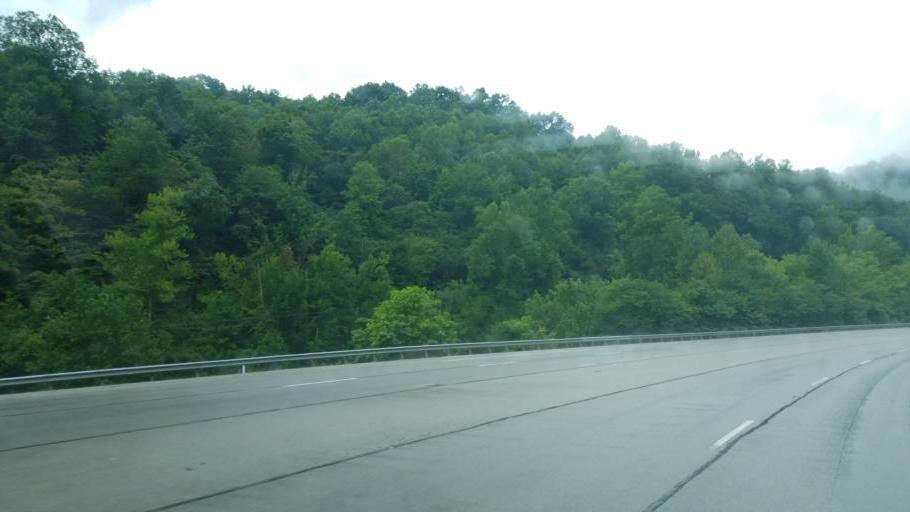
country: US
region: West Virginia
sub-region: Mingo County
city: Williamson
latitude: 37.6360
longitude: -82.2584
